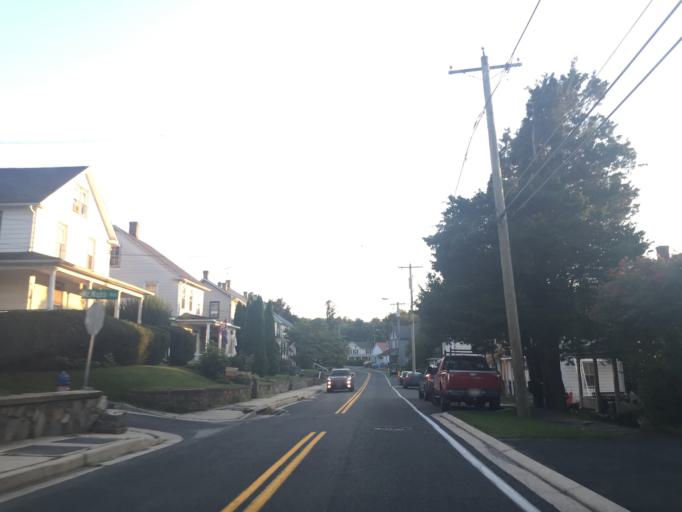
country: US
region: Pennsylvania
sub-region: York County
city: Susquehanna Trails
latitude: 39.7192
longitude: -76.3369
